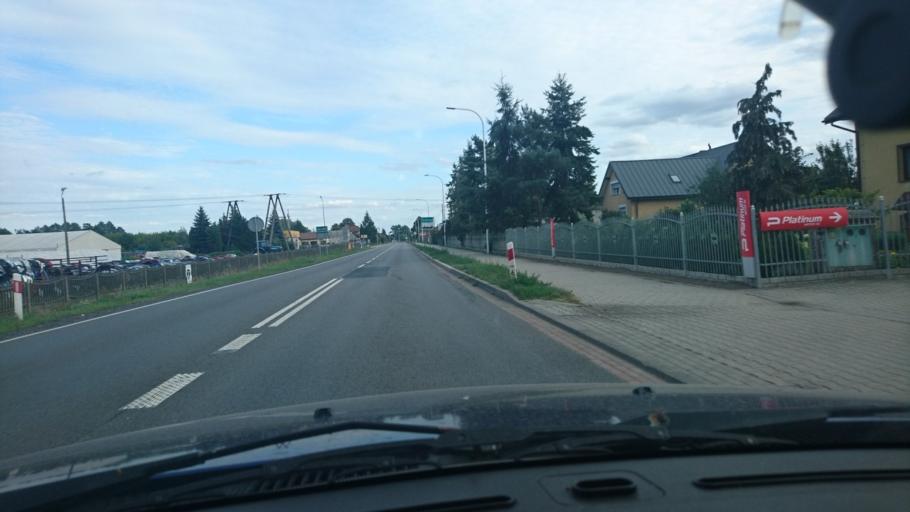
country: PL
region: Greater Poland Voivodeship
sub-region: Powiat kepinski
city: Kepno
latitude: 51.3099
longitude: 17.9863
